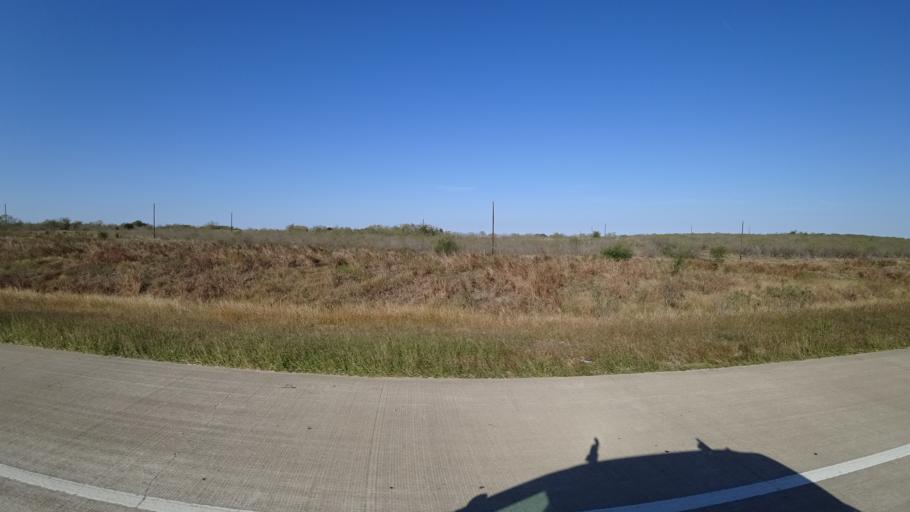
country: US
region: Texas
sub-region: Travis County
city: Onion Creek
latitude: 30.1067
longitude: -97.6667
